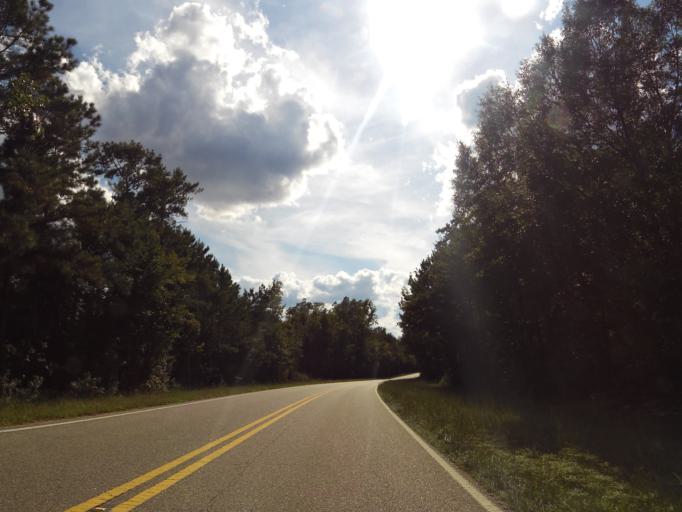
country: US
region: Alabama
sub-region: Dallas County
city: Selmont-West Selmont
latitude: 32.1603
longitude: -87.0614
